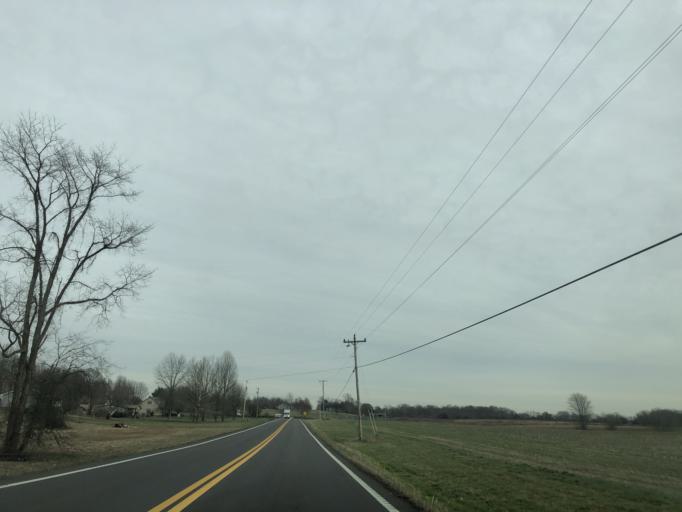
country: US
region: Tennessee
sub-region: Sumner County
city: White House
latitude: 36.4765
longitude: -86.7226
